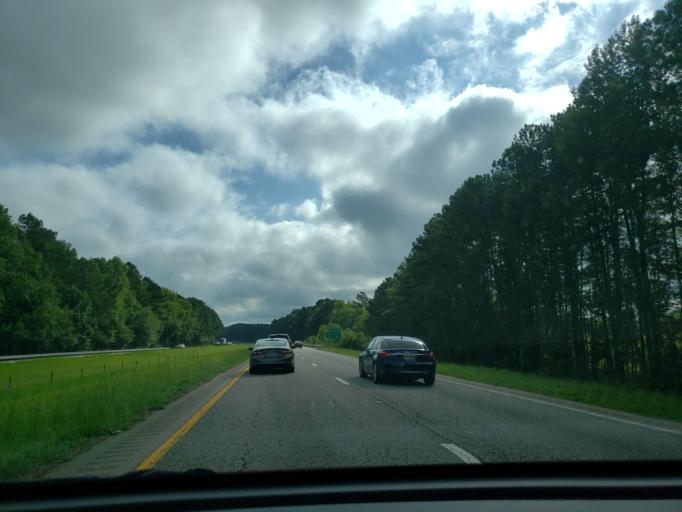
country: US
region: North Carolina
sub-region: Wake County
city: Zebulon
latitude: 35.8690
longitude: -78.2422
